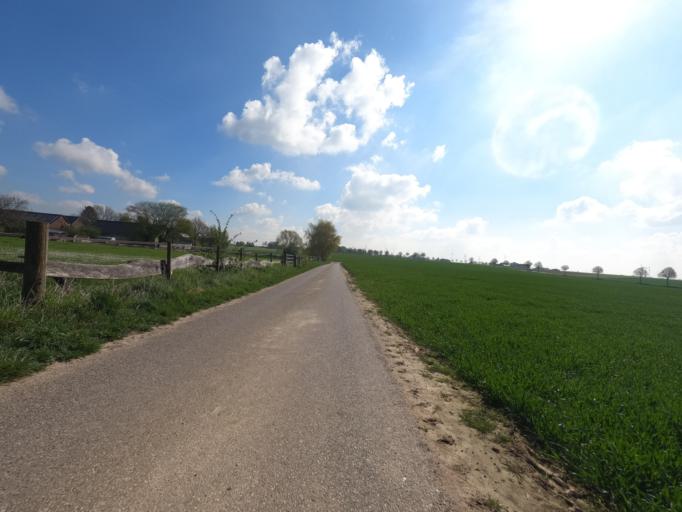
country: DE
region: North Rhine-Westphalia
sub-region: Regierungsbezirk Koln
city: Heinsberg
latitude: 51.0299
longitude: 6.0981
